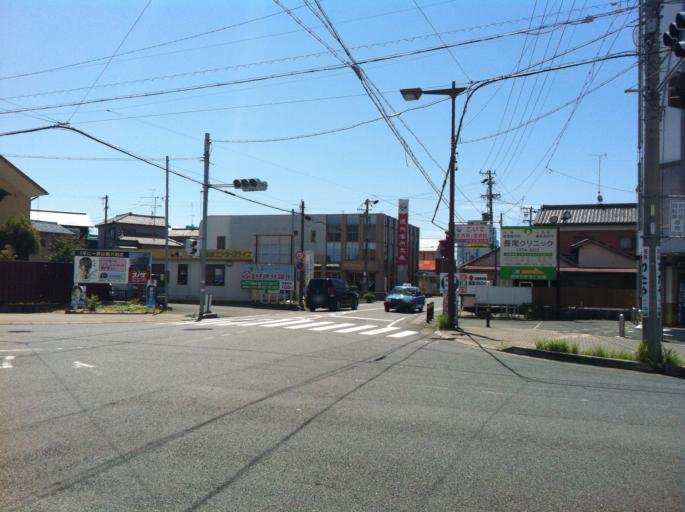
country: JP
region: Shizuoka
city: Kosai-shi
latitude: 34.7147
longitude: 137.5442
